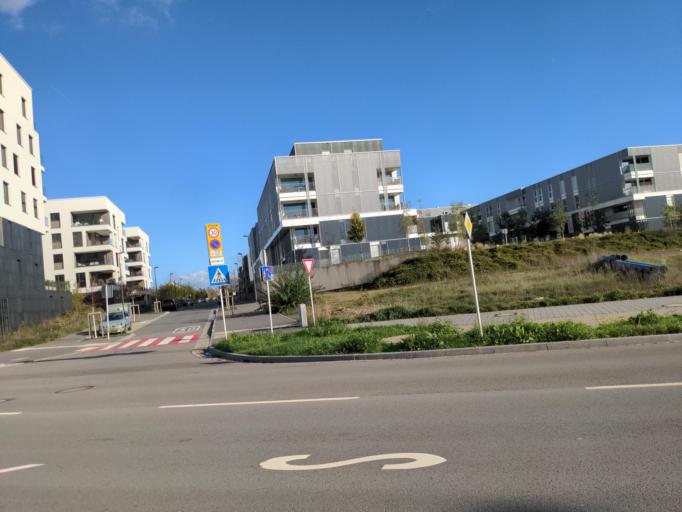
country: LU
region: Luxembourg
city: Kirchberg
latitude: 49.6348
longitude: 6.1597
